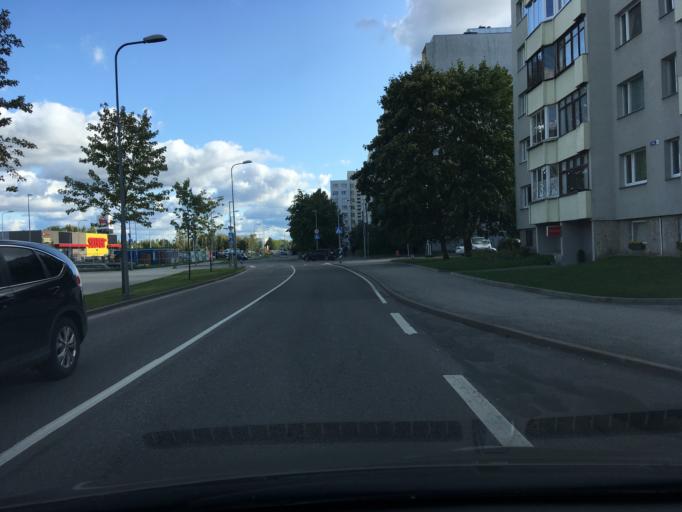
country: EE
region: Harju
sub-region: Tallinna linn
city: Kose
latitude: 59.4429
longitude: 24.8472
